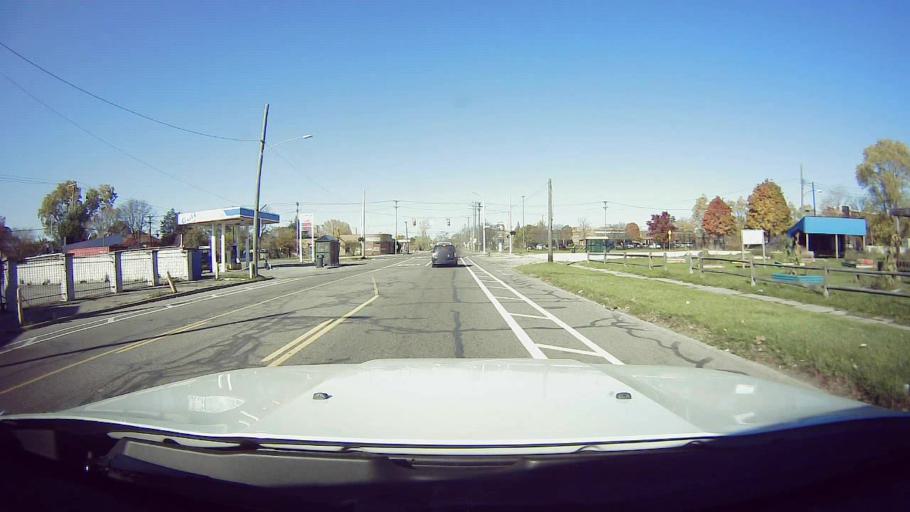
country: US
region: Michigan
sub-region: Wayne County
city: Highland Park
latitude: 42.3974
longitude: -83.1249
